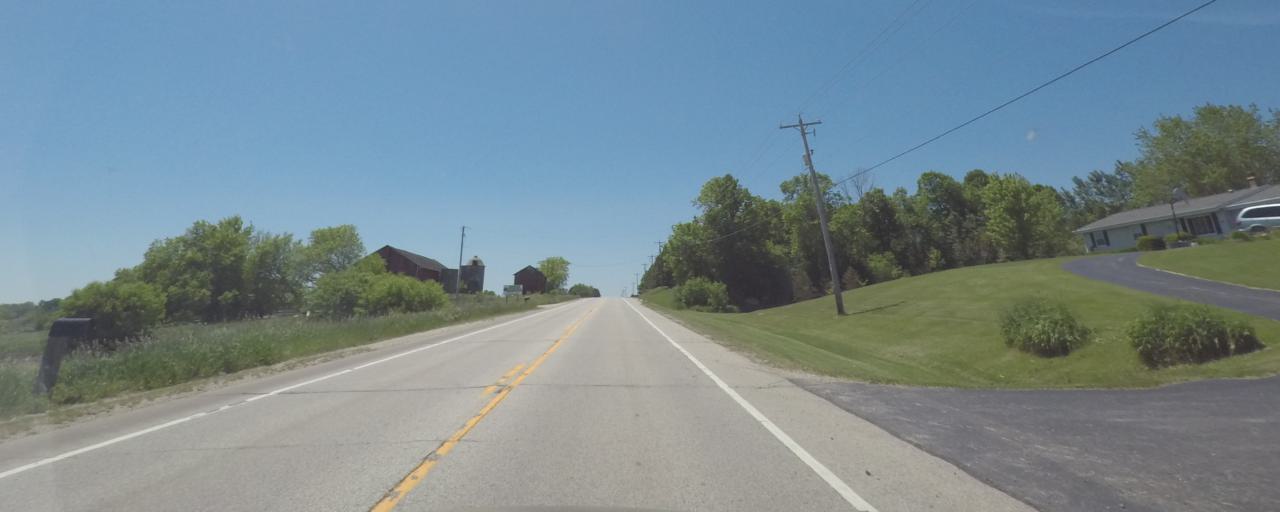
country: US
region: Wisconsin
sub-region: Ozaukee County
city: Kohler
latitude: 43.5649
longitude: -88.0681
